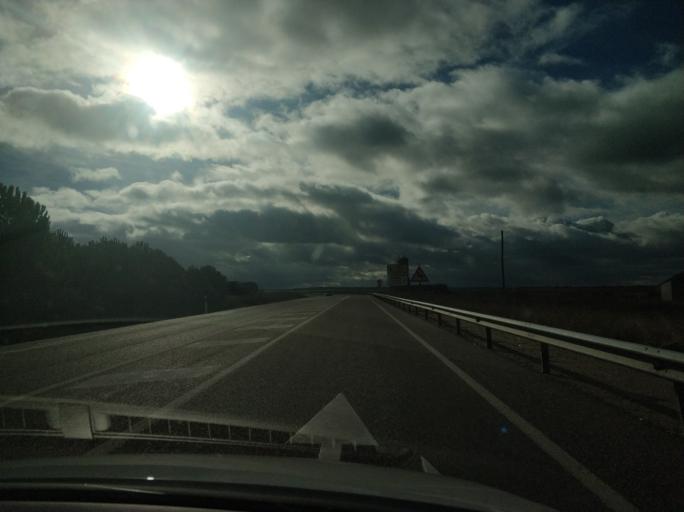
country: ES
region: Castille and Leon
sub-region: Provincia de Segovia
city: Ayllon
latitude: 41.4088
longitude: -3.4151
